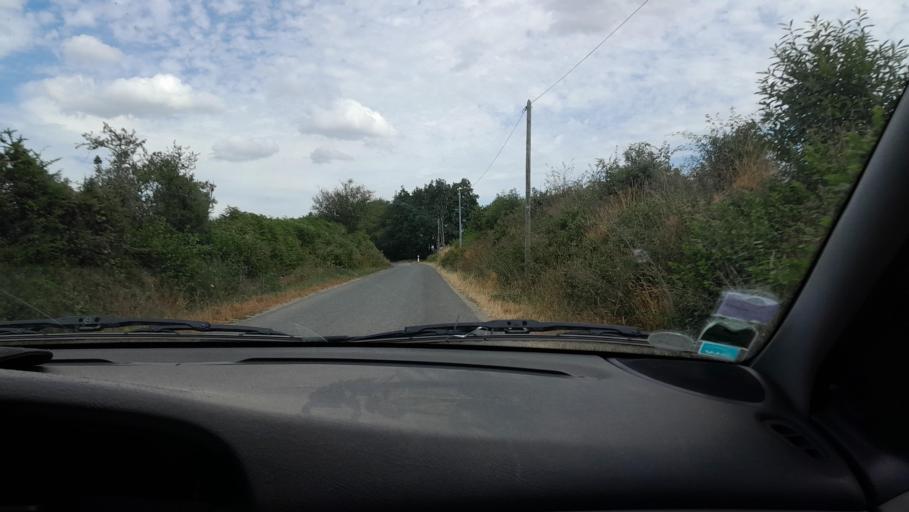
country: FR
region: Pays de la Loire
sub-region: Departement de la Mayenne
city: Juvigne
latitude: 48.1848
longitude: -1.0339
